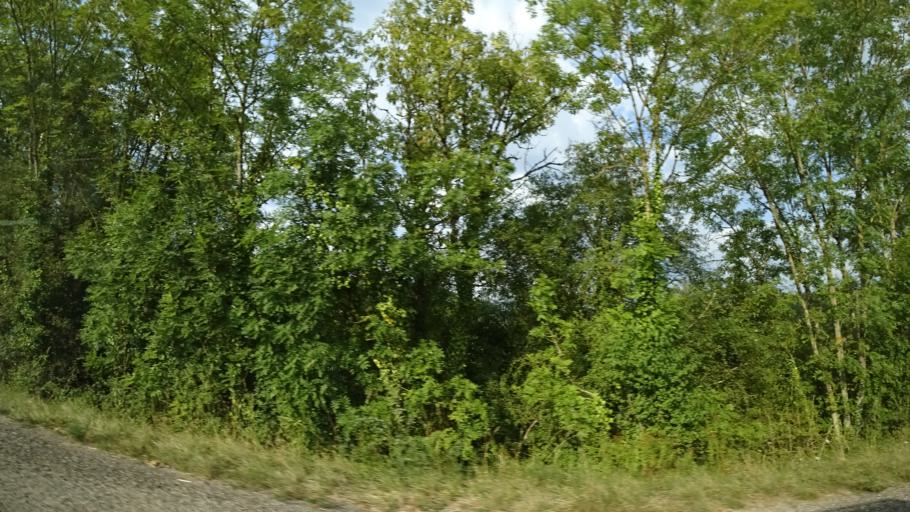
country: FR
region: Midi-Pyrenees
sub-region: Departement de l'Aveyron
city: Saint-Christophe-Vallon
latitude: 44.4787
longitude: 2.4060
